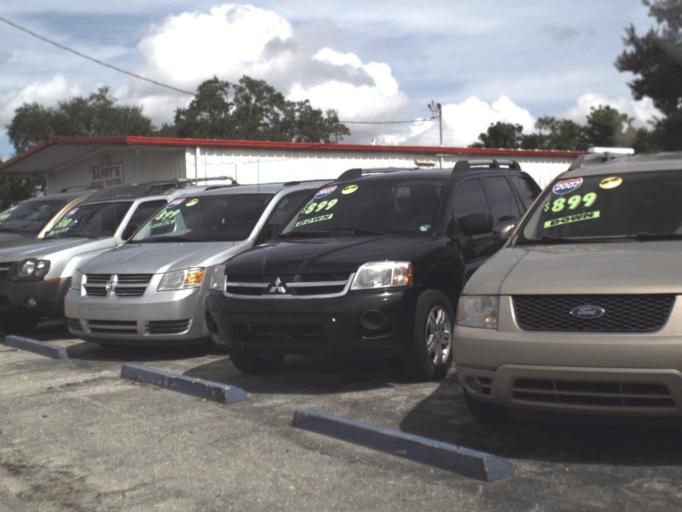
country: US
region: Florida
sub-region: Lee County
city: Fort Myers
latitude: 26.6275
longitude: -81.8620
